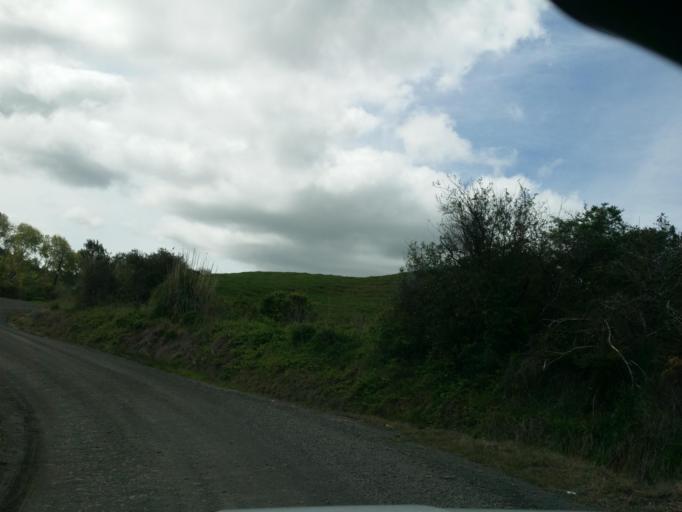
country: NZ
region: Northland
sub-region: Kaipara District
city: Dargaville
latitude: -35.8781
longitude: 174.0406
